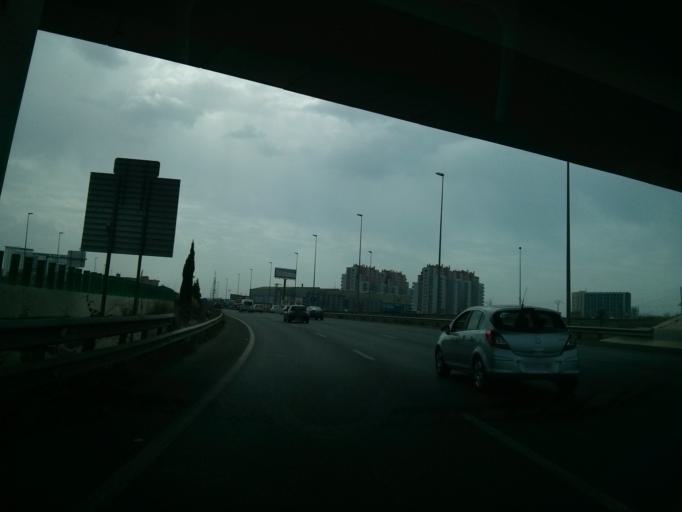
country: ES
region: Valencia
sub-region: Provincia de Valencia
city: Burjassot
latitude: 39.5027
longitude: -0.3949
